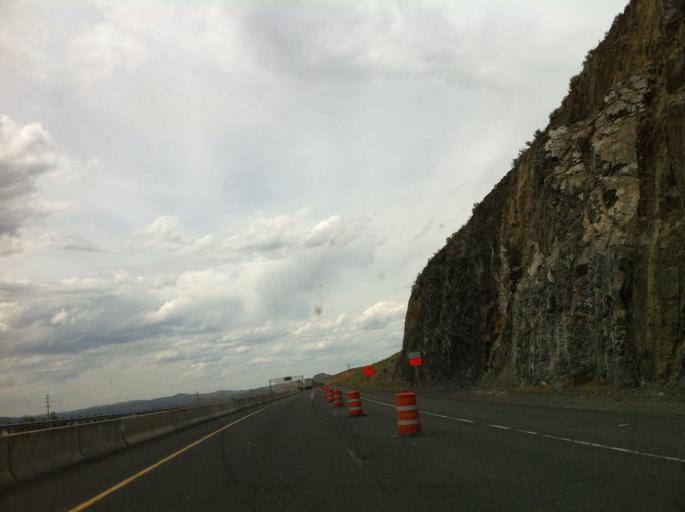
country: US
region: Oregon
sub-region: Baker County
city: Baker City
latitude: 44.5416
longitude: -117.4174
